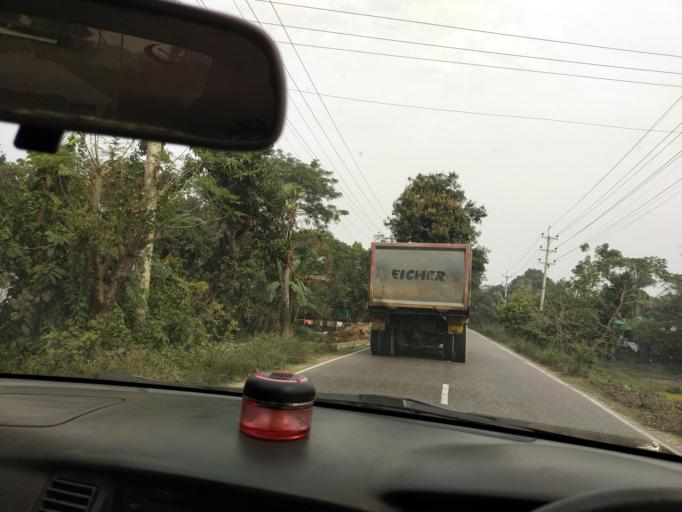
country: BD
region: Dhaka
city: Narsingdi
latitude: 24.0211
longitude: 90.7380
